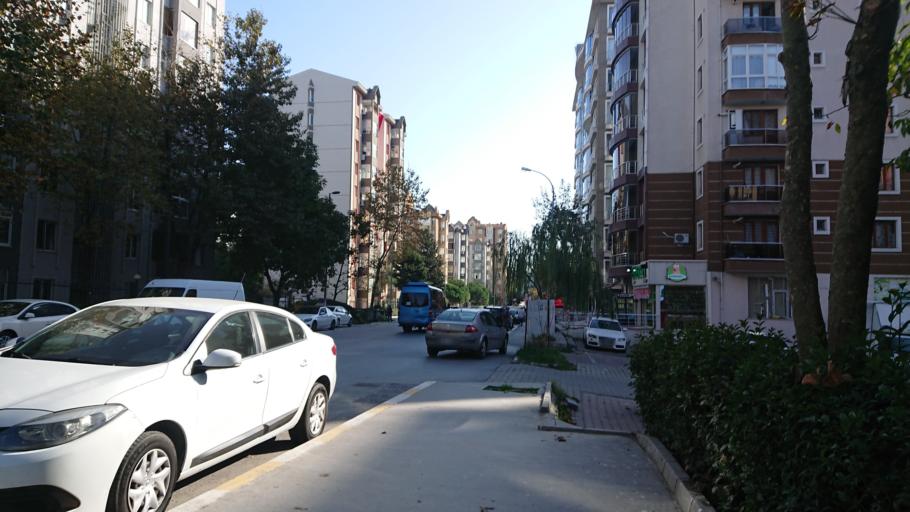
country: TR
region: Istanbul
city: Esenyurt
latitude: 41.0600
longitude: 28.6722
